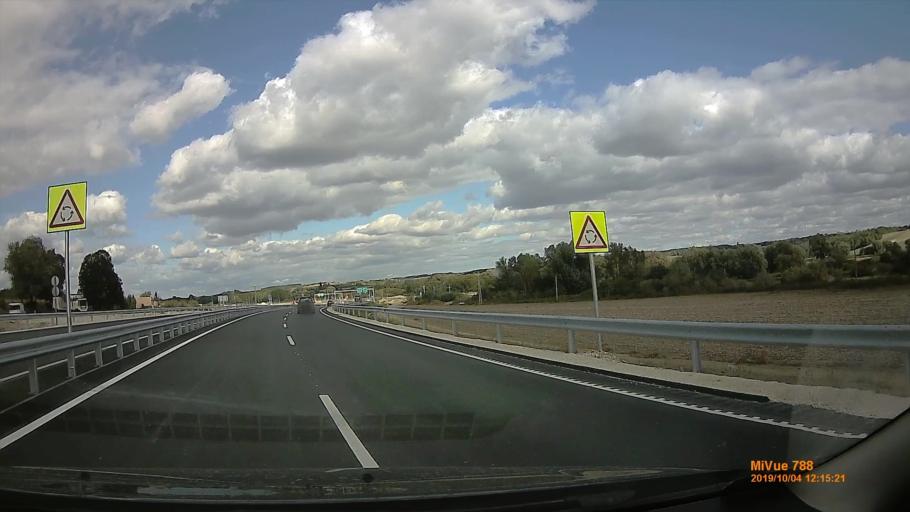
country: HU
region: Somogy
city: Karad
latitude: 46.5478
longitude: 17.8139
